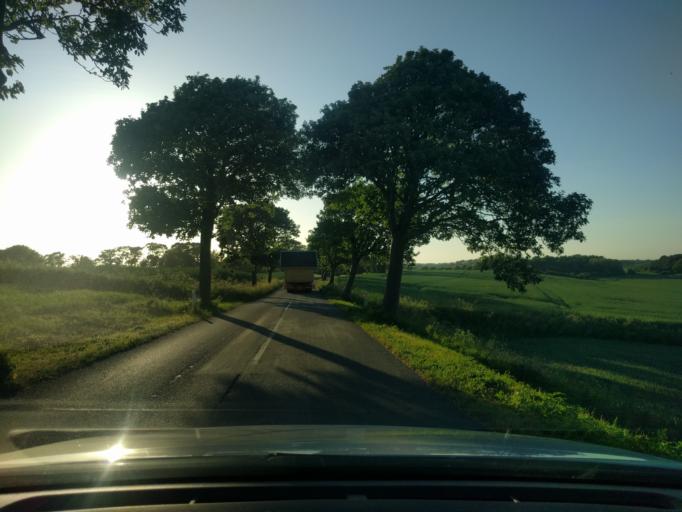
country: DK
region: South Denmark
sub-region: Kerteminde Kommune
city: Kerteminde
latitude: 55.5840
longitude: 10.6345
